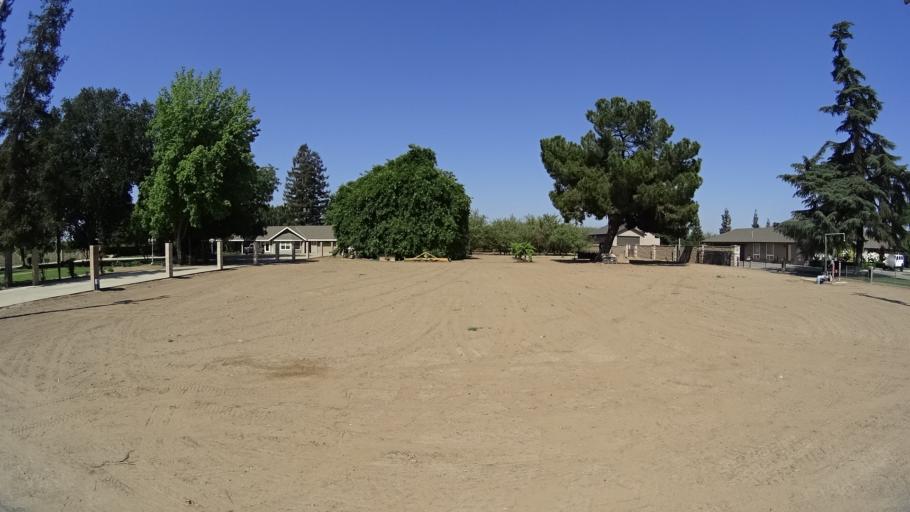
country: US
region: California
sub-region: Fresno County
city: Kingsburg
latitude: 36.4567
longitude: -119.5511
